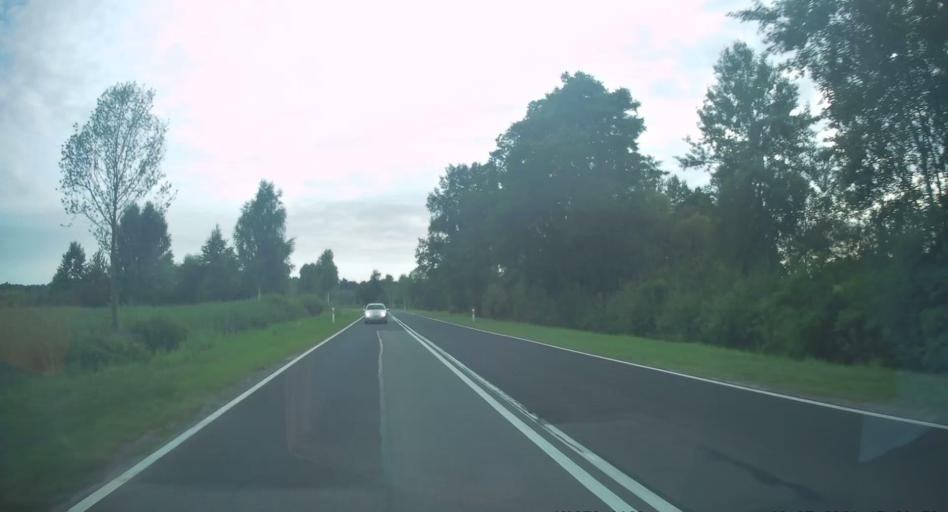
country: PL
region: Lodz Voivodeship
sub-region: Powiat radomszczanski
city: Plawno
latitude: 51.0175
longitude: 19.4254
